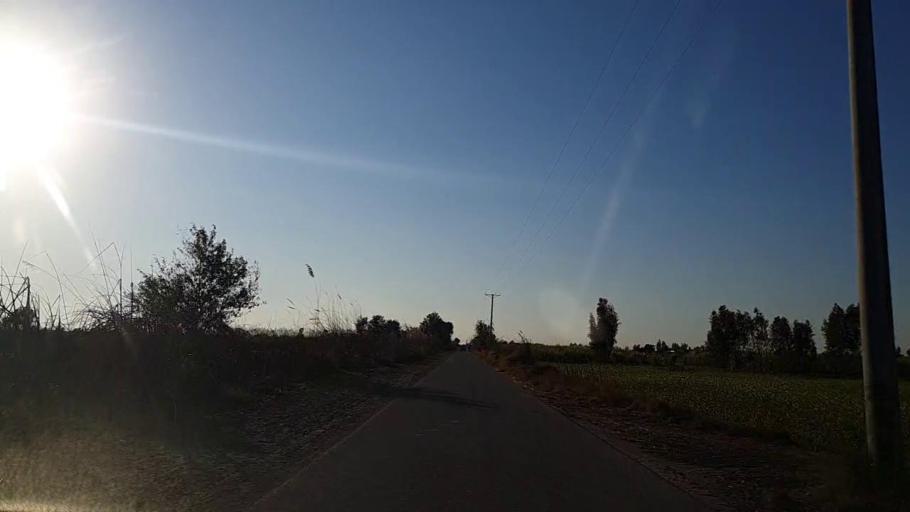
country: PK
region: Sindh
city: Khadro
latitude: 26.2790
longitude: 68.8922
